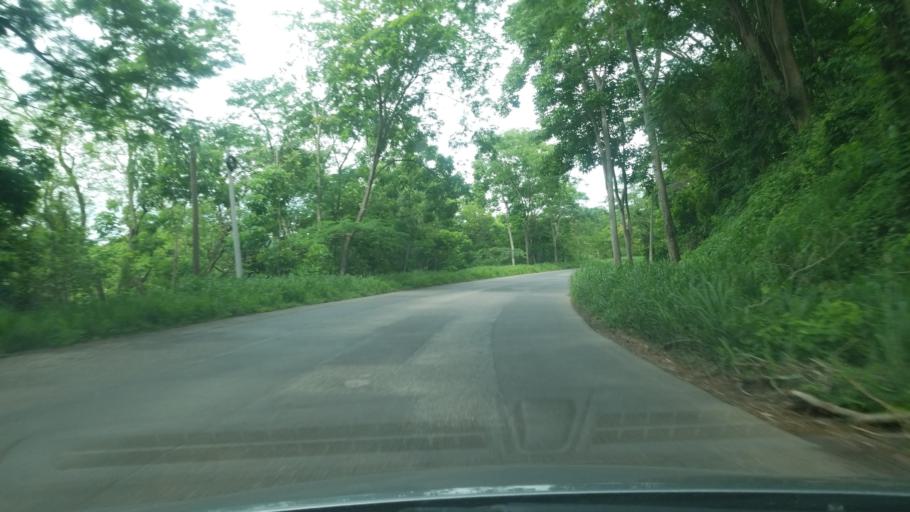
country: HN
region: Santa Barbara
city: Camalote
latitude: 15.3224
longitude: -88.3117
